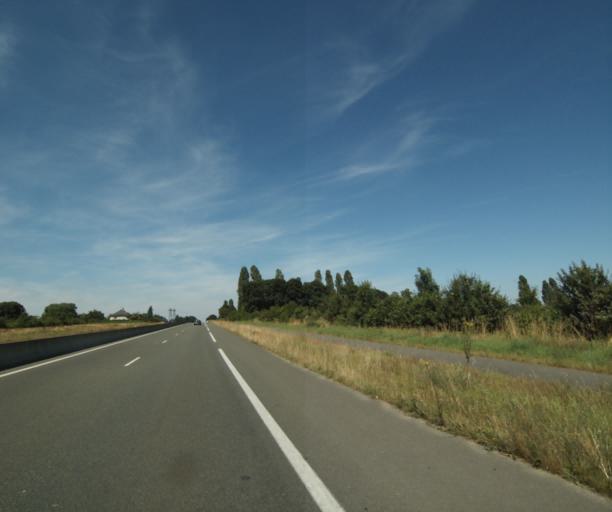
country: FR
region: Pays de la Loire
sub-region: Departement de la Mayenne
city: Laval
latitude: 48.0463
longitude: -0.7987
